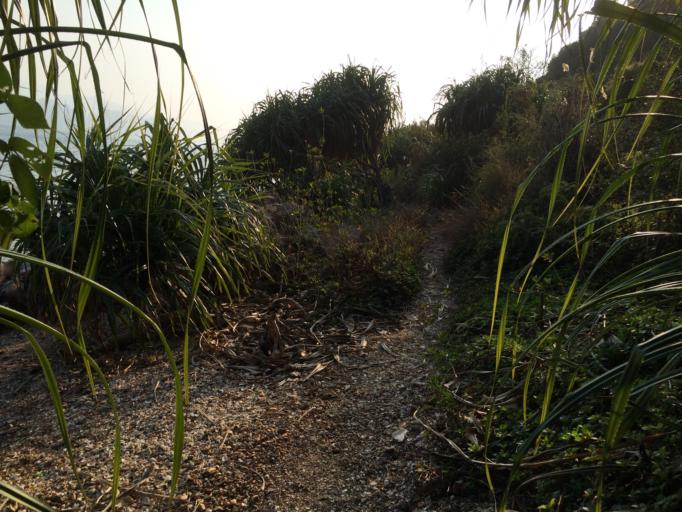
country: HK
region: Tai Po
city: Tai Po
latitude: 22.4544
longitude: 114.2331
